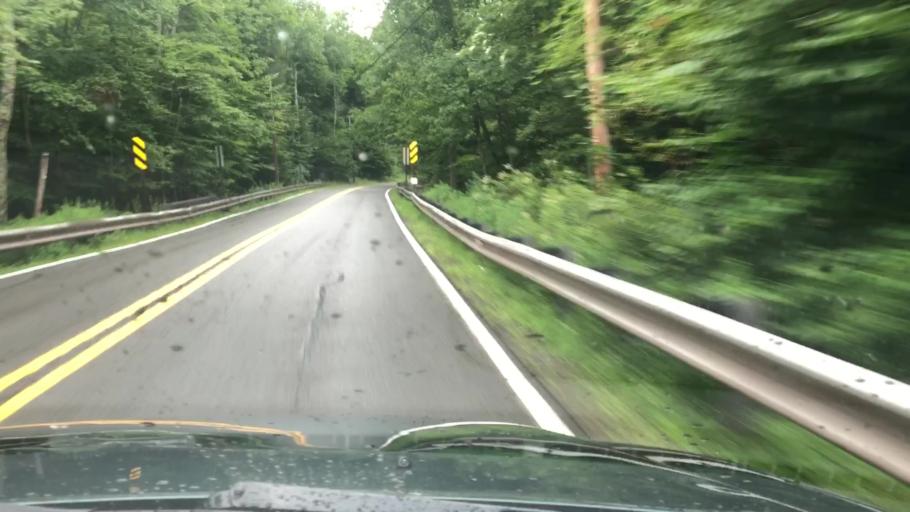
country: US
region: Pennsylvania
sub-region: Monroe County
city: Mountainhome
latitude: 41.2787
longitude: -75.2474
